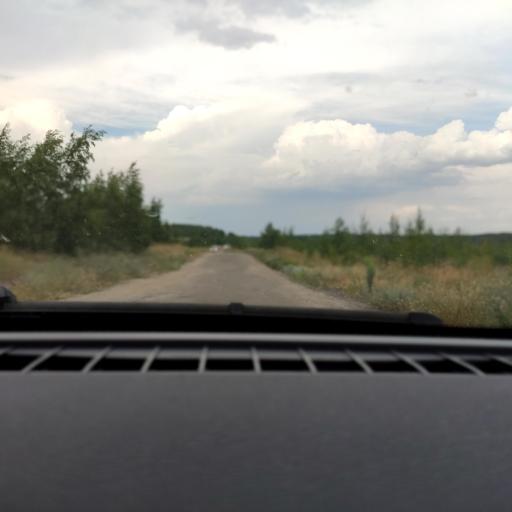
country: RU
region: Voronezj
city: Somovo
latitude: 51.7698
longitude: 39.3340
